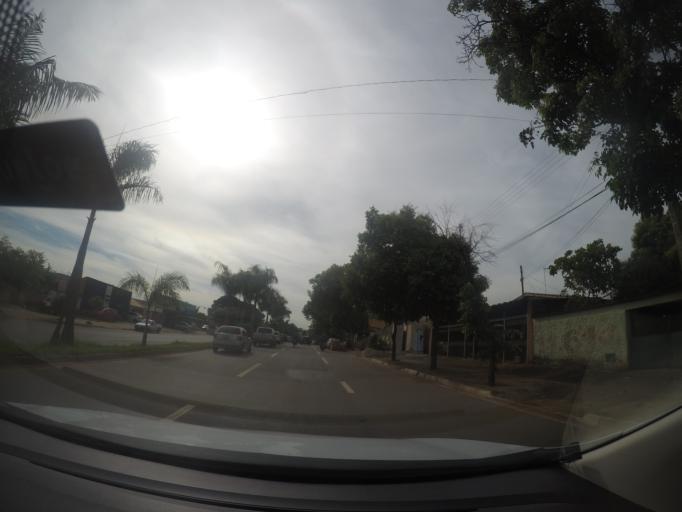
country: BR
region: Goias
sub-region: Goiania
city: Goiania
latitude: -16.6569
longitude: -49.2975
